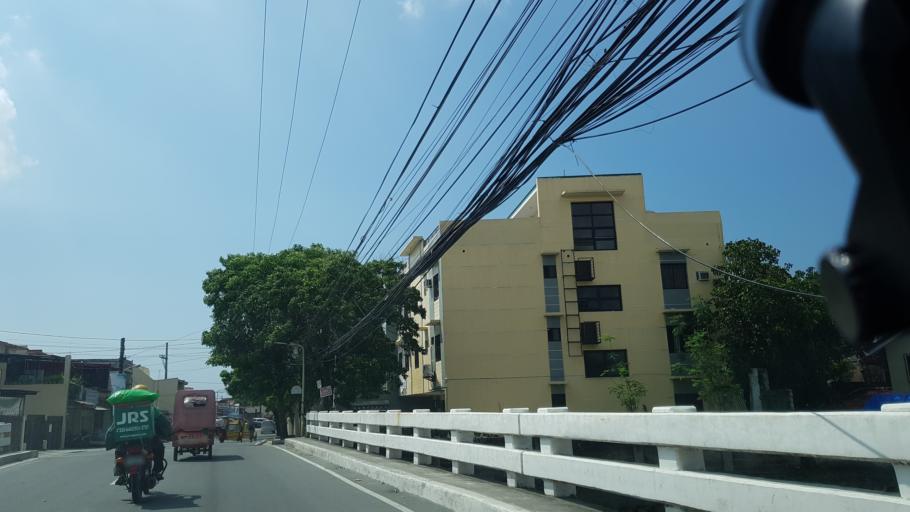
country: PH
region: Calabarzon
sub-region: Province of Rizal
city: Las Pinas
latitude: 14.4651
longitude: 120.9843
